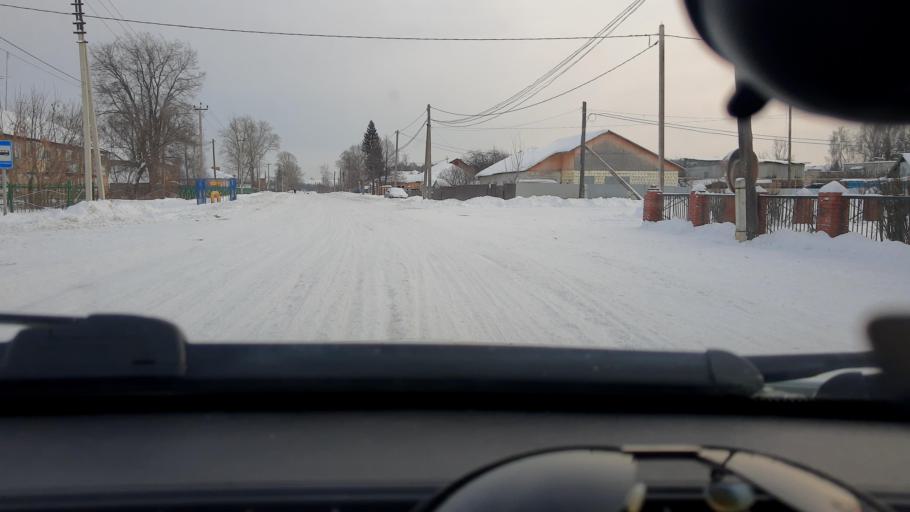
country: RU
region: Bashkortostan
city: Yazykovo
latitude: 55.0465
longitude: 56.1801
